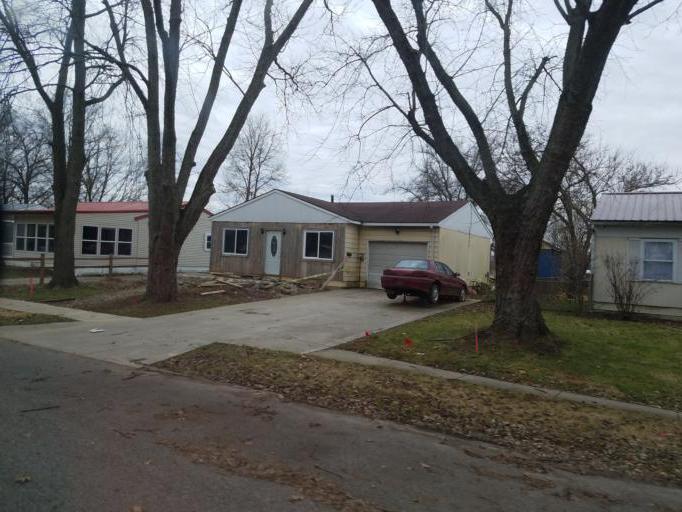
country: US
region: Ohio
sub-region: Marion County
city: Marion
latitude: 40.6126
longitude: -83.1213
